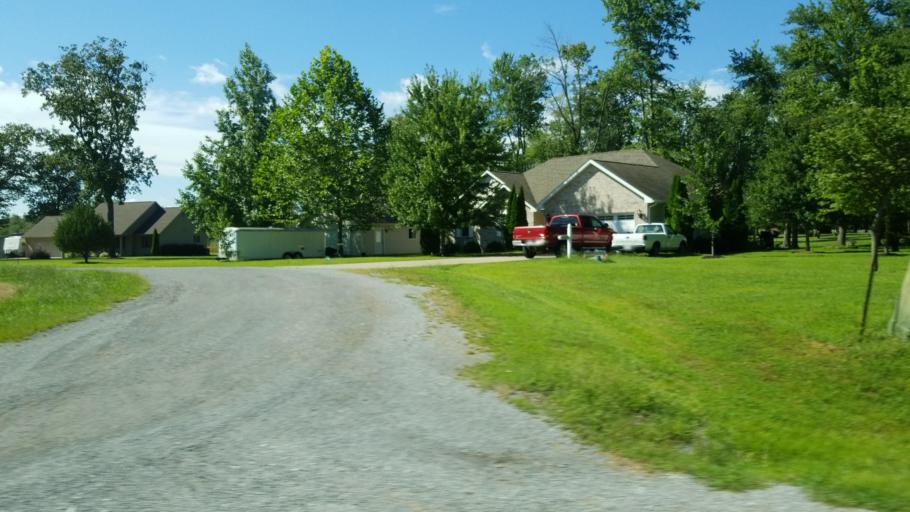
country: US
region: Illinois
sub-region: Williamson County
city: Marion
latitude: 37.7618
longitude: -88.8650
